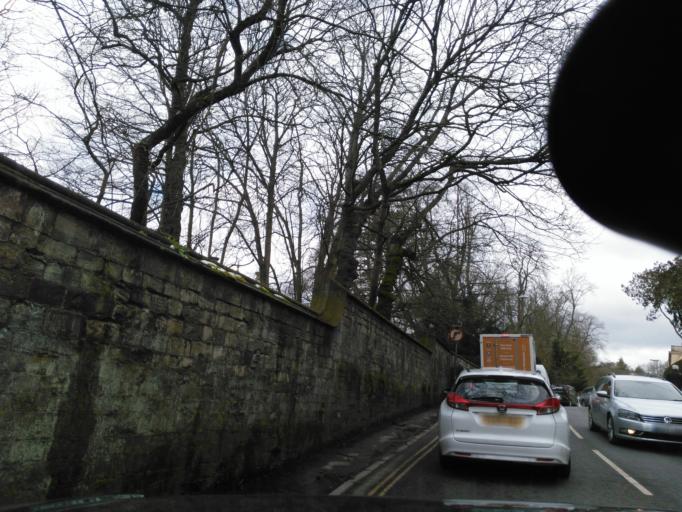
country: GB
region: England
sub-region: Wiltshire
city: Bradford-on-Avon
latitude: 51.3470
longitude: -2.2463
